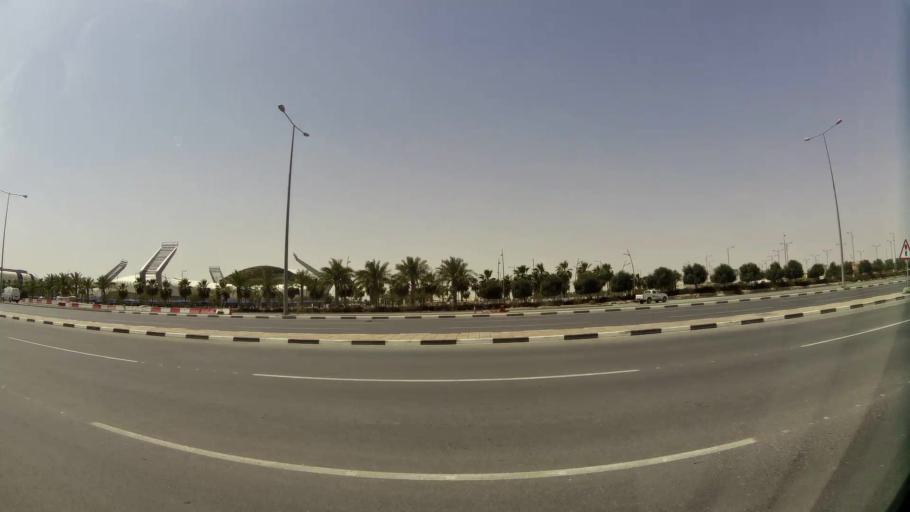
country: QA
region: Baladiyat Umm Salal
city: Umm Salal Muhammad
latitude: 25.3756
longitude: 51.4710
